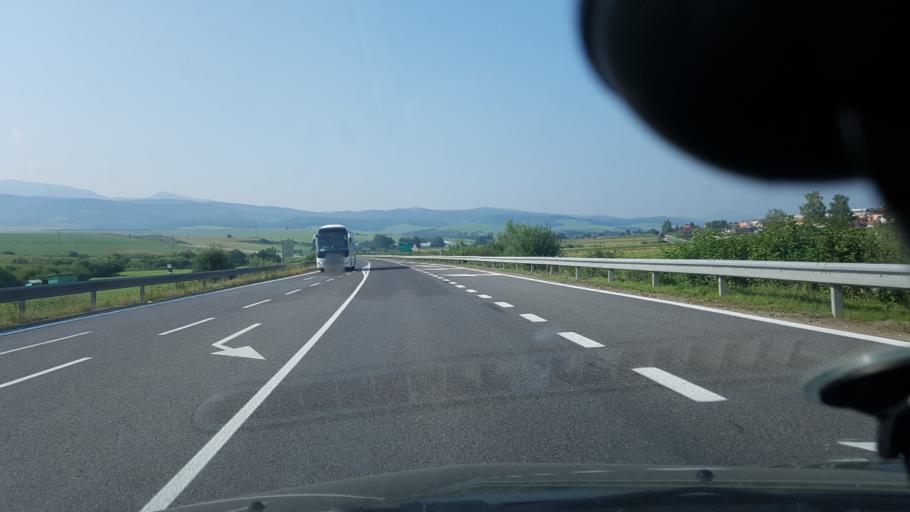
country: SK
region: Zilinsky
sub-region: Okres Zilina
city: Trstena
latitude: 49.3779
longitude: 19.6305
